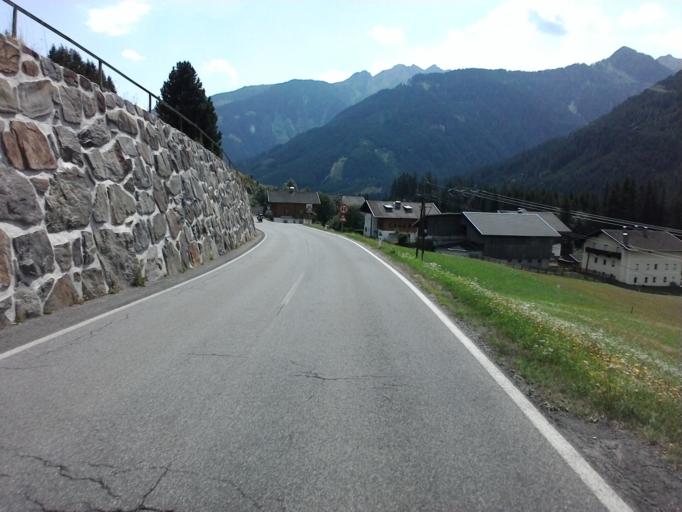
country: AT
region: Tyrol
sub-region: Politischer Bezirk Lienz
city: Obertilliach
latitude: 46.7043
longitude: 12.6404
